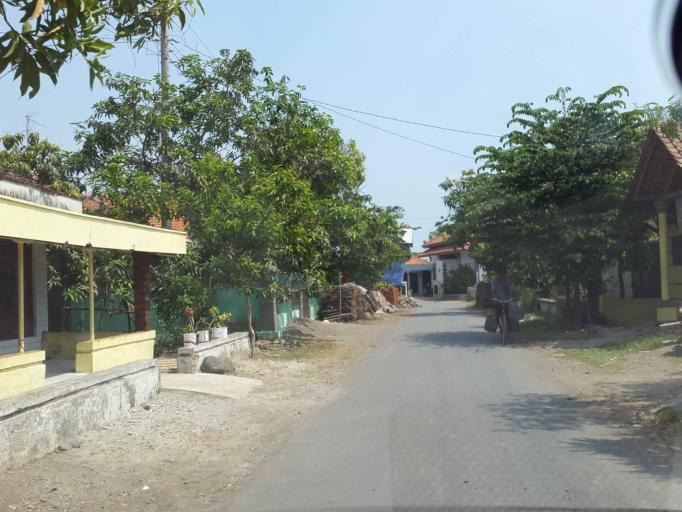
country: ID
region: Central Java
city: Dukuhturi
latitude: -6.8313
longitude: 109.0569
